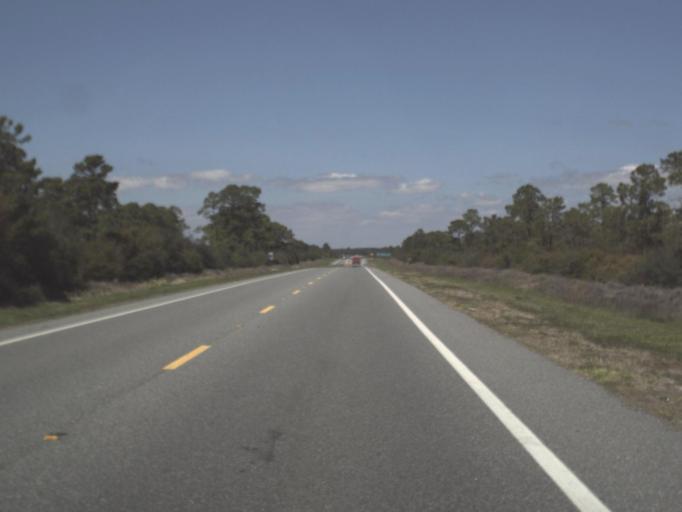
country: US
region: Florida
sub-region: Gulf County
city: Port Saint Joe
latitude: 29.8569
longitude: -85.3357
